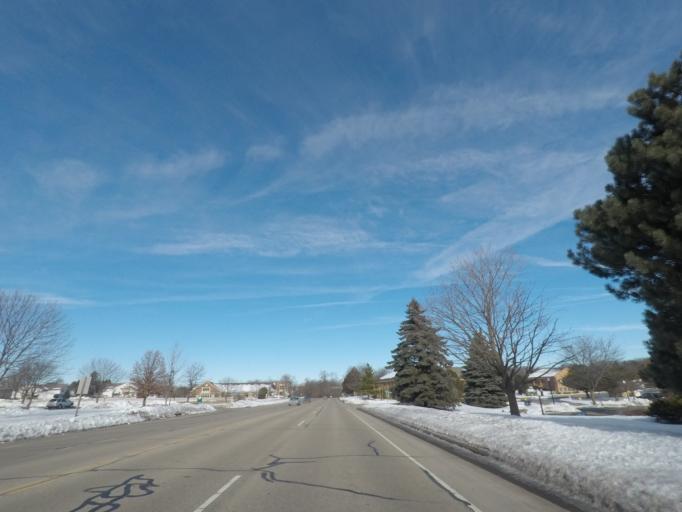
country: US
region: Wisconsin
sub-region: Dane County
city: Fitchburg
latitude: 43.0137
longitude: -89.4558
